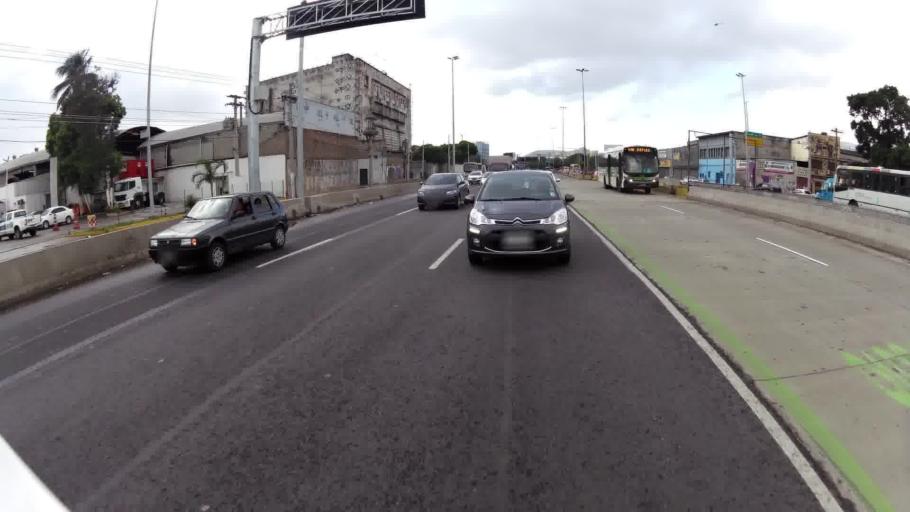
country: BR
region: Rio de Janeiro
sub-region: Rio De Janeiro
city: Rio de Janeiro
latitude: -22.8868
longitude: -43.2245
